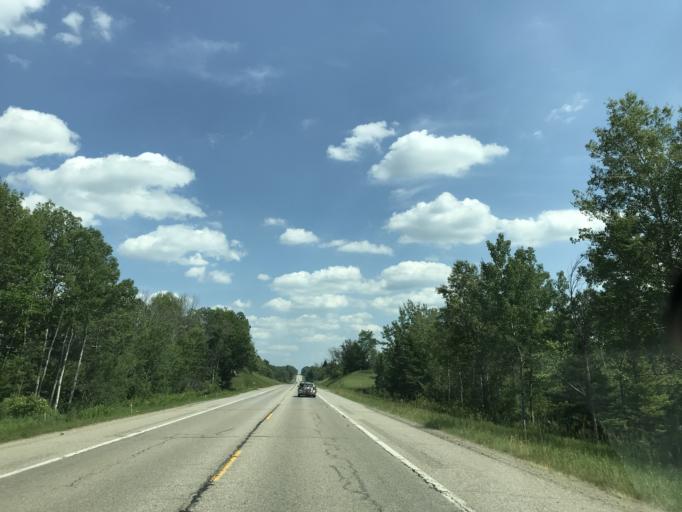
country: US
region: Michigan
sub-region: Osceola County
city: Evart
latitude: 44.0930
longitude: -85.2371
